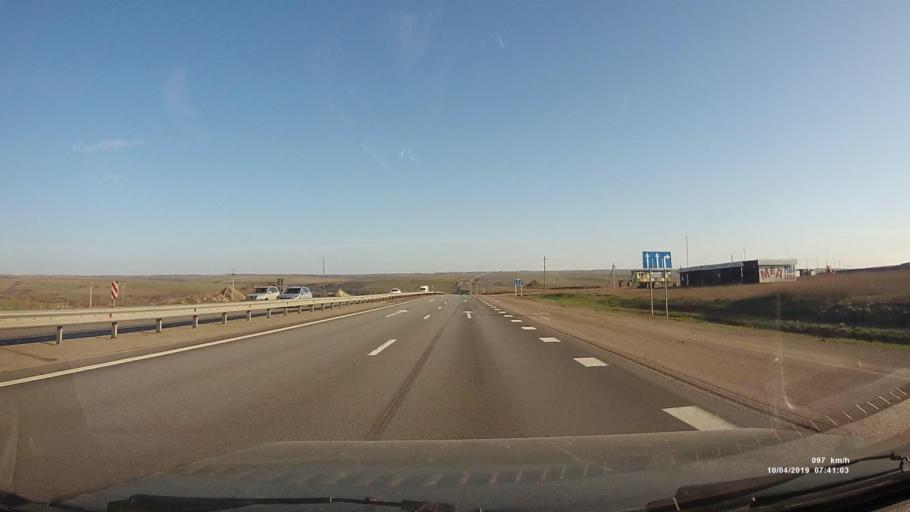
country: RU
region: Rostov
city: Likhoy
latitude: 48.1276
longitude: 40.2598
